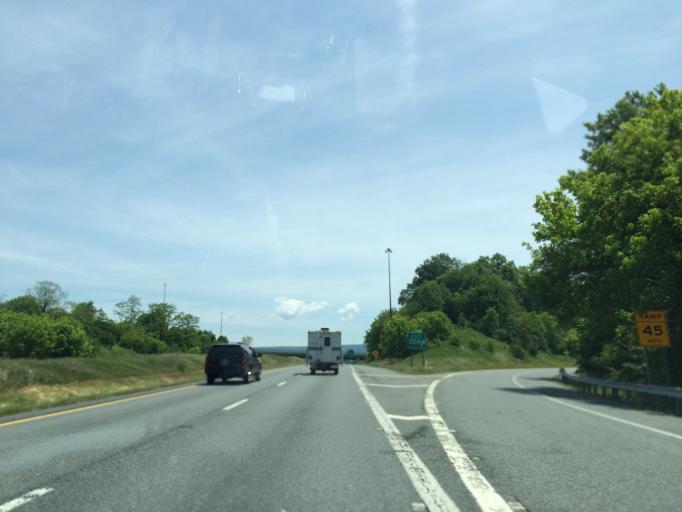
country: US
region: Maryland
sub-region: Washington County
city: Robinwood
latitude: 39.5996
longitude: -77.6872
